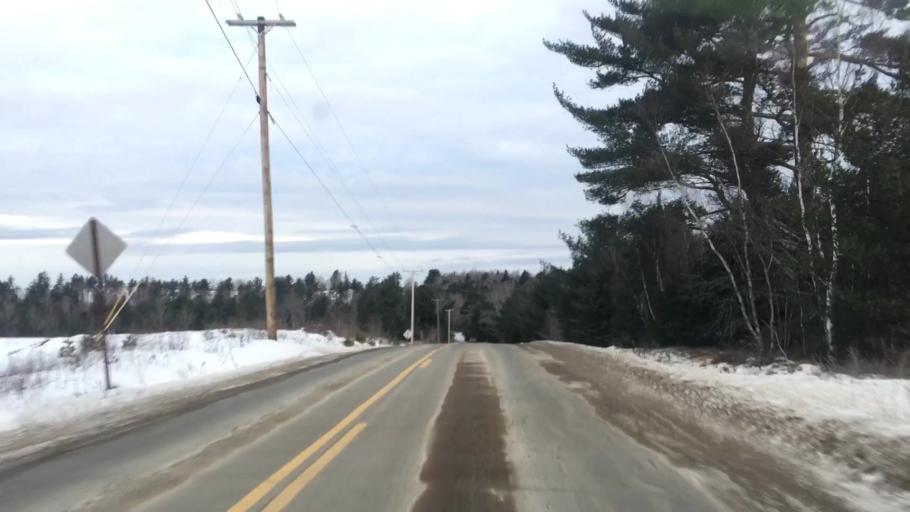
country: US
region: Maine
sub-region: Hancock County
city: Franklin
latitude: 44.8382
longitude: -68.3226
